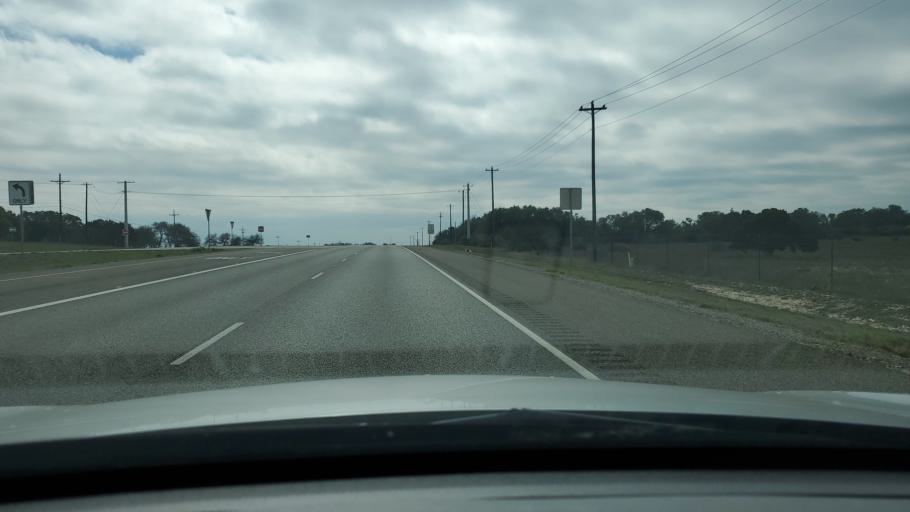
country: US
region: Texas
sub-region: Williamson County
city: Florence
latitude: 30.8081
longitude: -97.7717
